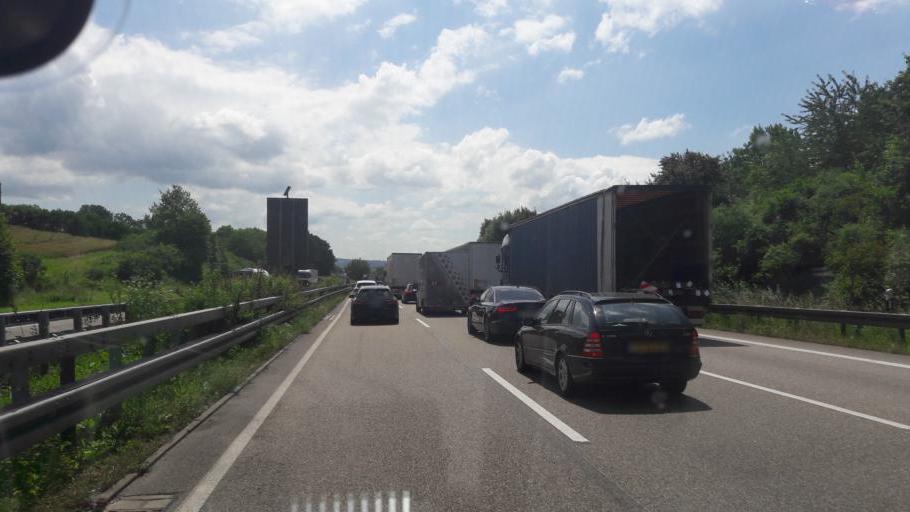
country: DE
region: Baden-Wuerttemberg
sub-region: Regierungsbezirk Stuttgart
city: Bretzfeld
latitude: 49.1859
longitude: 9.4159
